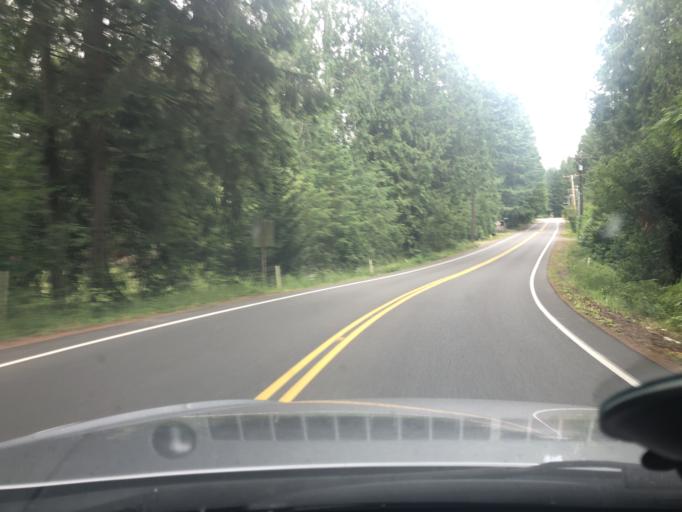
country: US
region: Washington
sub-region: King County
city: Lake Morton-Berrydale
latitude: 47.3007
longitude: -122.0917
